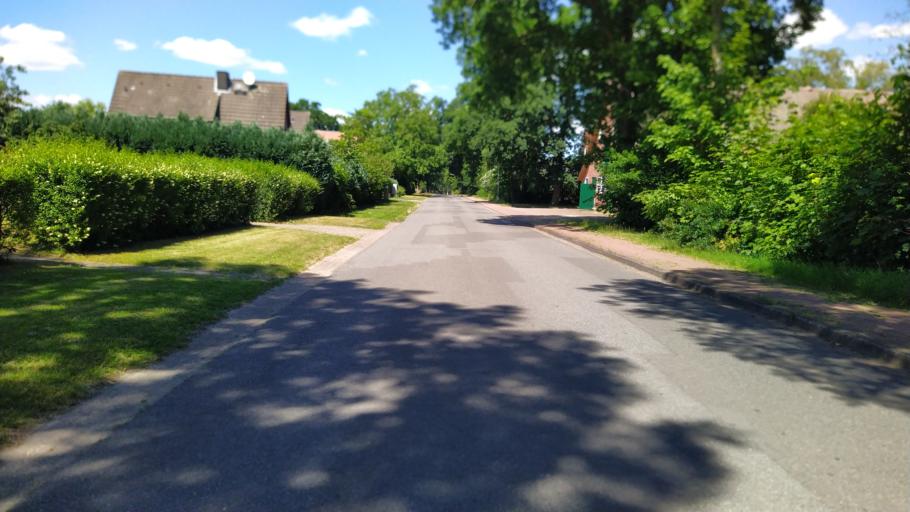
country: DE
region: Lower Saxony
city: Estorf
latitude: 53.5717
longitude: 9.2035
